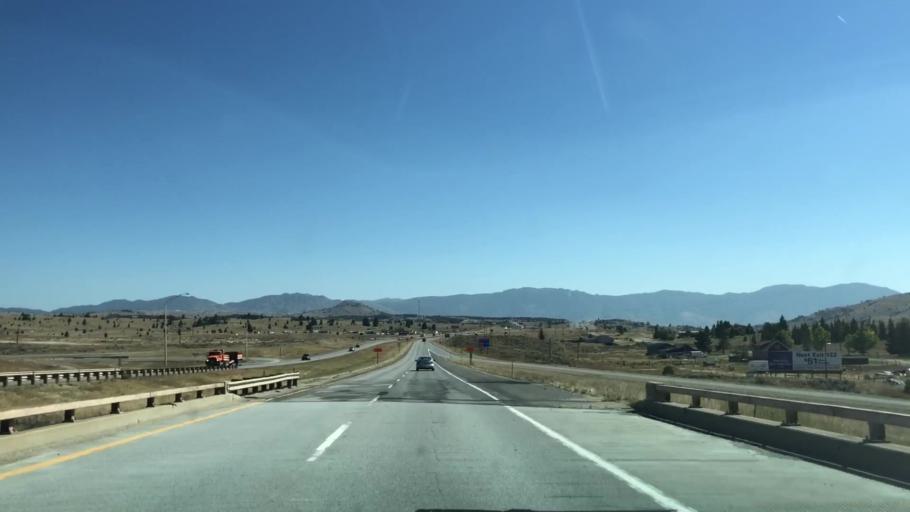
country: US
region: Montana
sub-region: Silver Bow County
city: Butte
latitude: 46.0080
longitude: -112.6380
